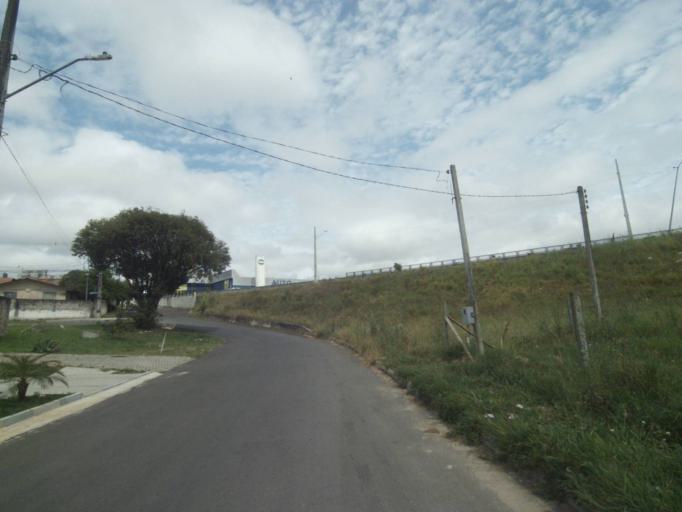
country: BR
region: Parana
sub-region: Pinhais
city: Pinhais
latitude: -25.4343
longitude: -49.2318
